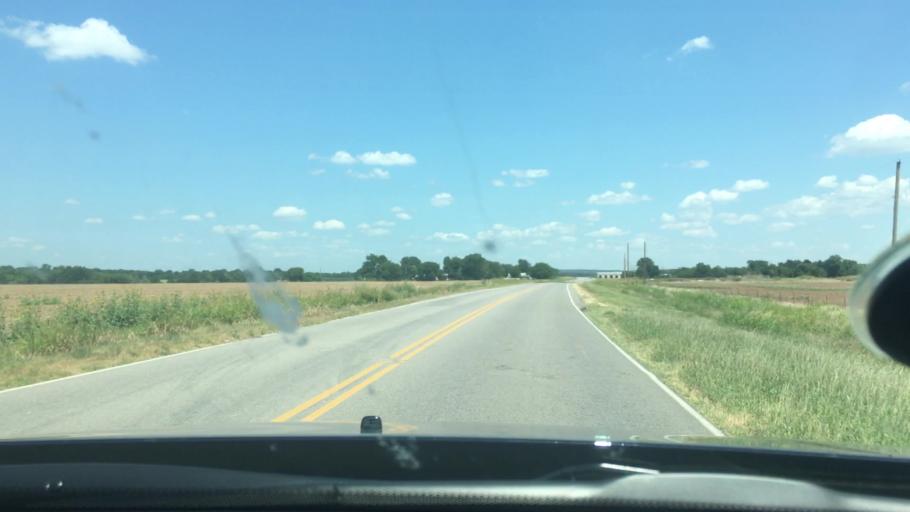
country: US
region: Oklahoma
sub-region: Carter County
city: Dickson
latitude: 34.2257
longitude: -96.9771
